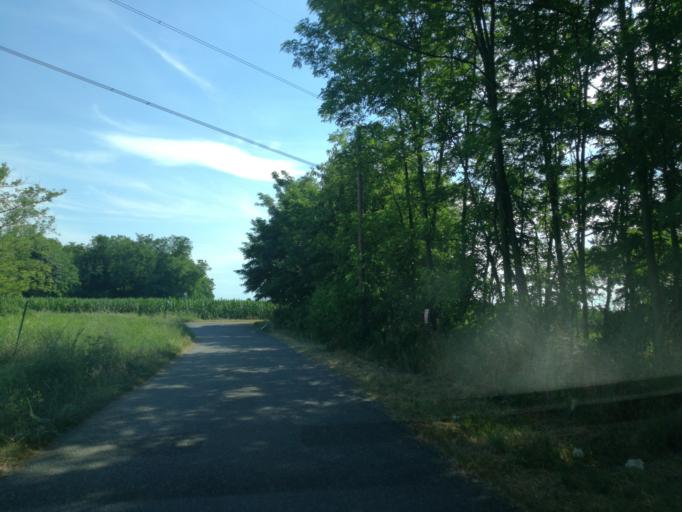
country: IT
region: Lombardy
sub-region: Provincia di Lecco
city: Verderio Inferiore
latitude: 45.6600
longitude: 9.4241
